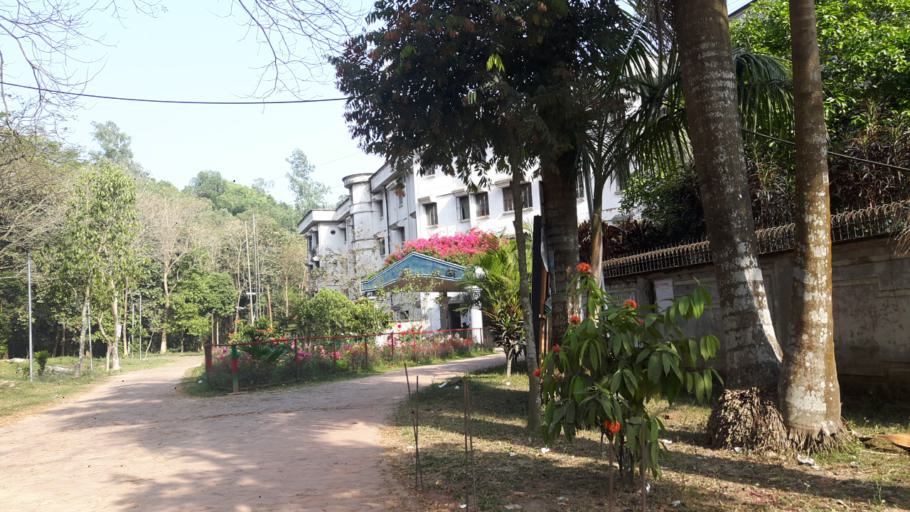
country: BD
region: Chittagong
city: Chittagong
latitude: 22.4695
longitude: 91.7896
